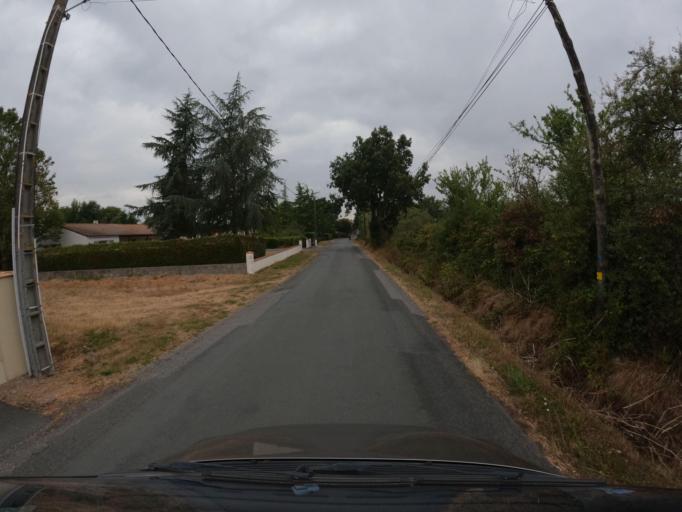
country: FR
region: Pays de la Loire
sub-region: Departement de la Vendee
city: La Guyonniere
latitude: 46.9678
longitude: -1.2719
